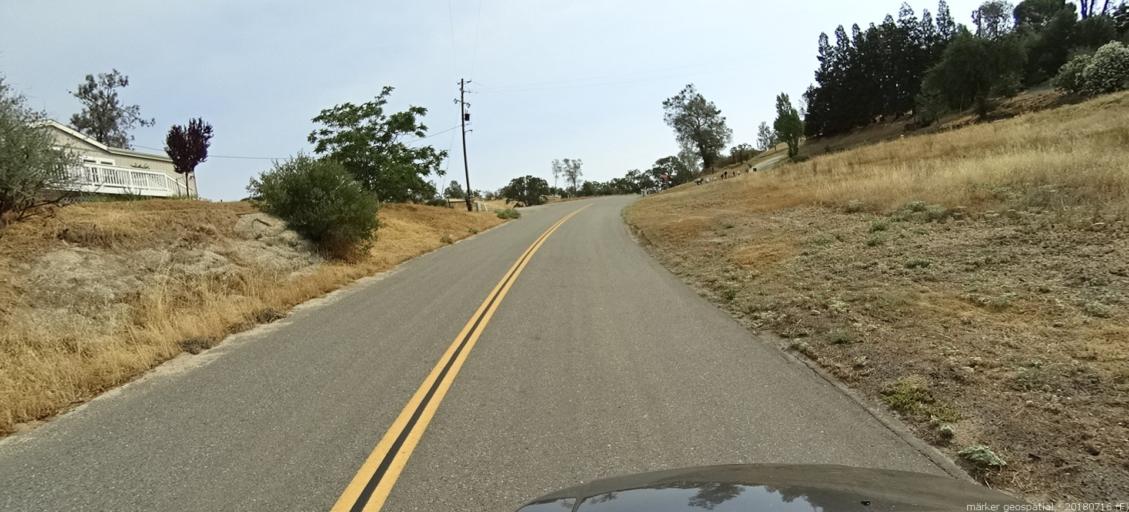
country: US
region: California
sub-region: Madera County
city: Yosemite Lakes
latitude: 37.1622
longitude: -119.8460
